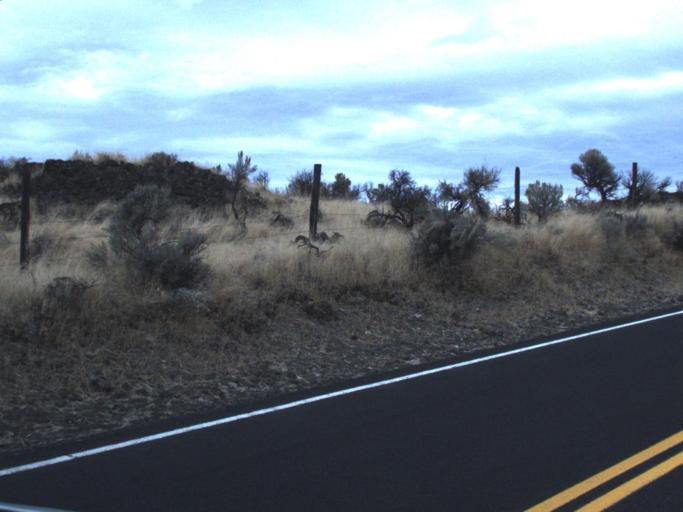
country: US
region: Washington
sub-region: Adams County
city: Ritzville
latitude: 47.4670
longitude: -118.7706
